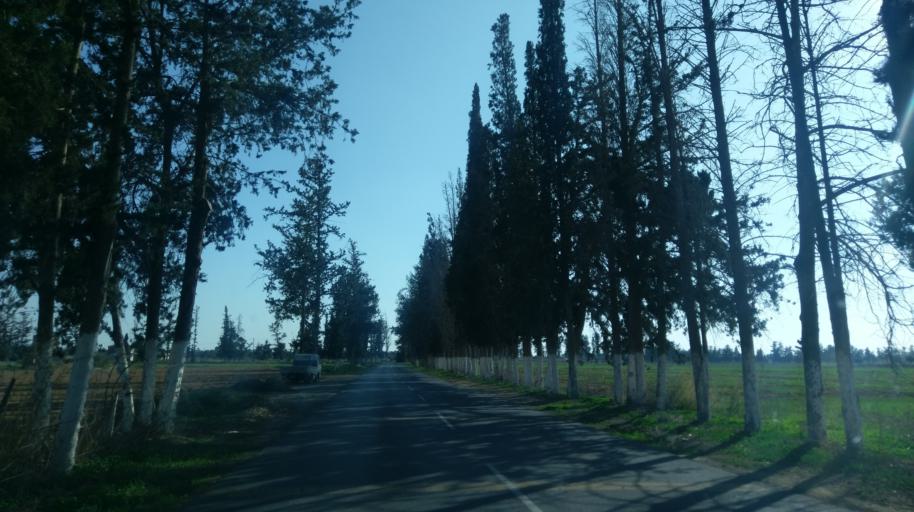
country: CY
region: Larnaka
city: Pergamos
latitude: 35.1093
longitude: 33.7281
